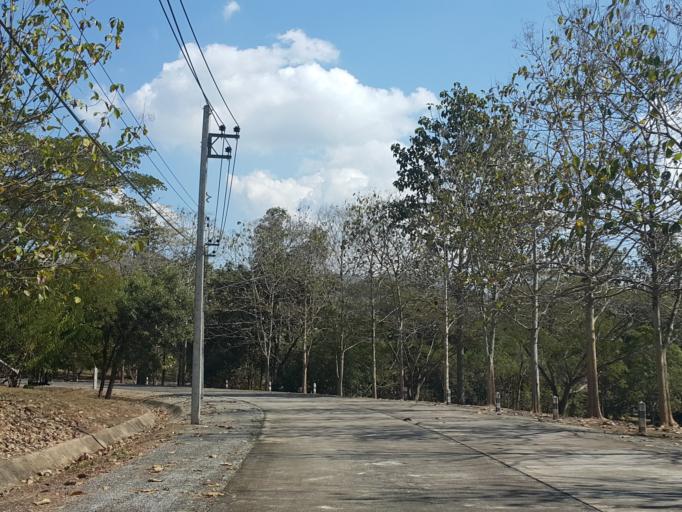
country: TH
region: Chiang Mai
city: Mae Taeng
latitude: 19.0218
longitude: 98.9919
